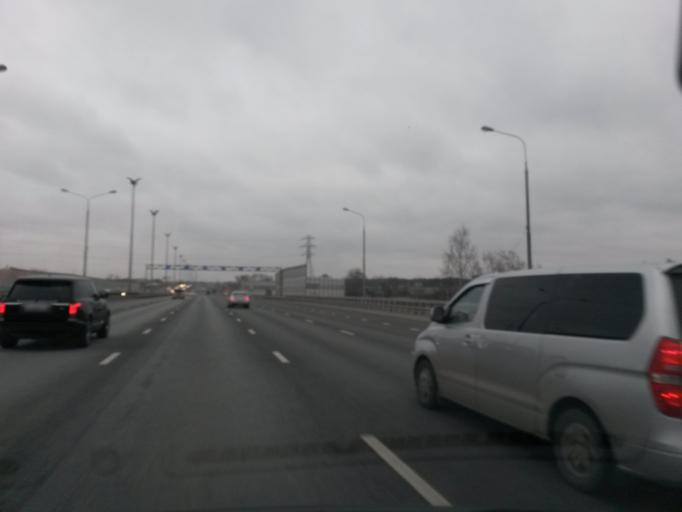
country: RU
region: Moskovskaya
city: Bolshevo
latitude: 55.9588
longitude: 37.8333
